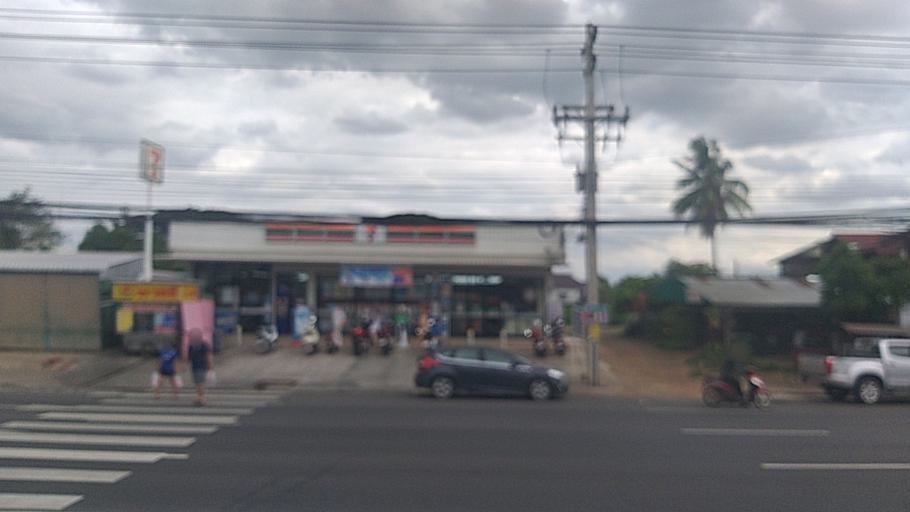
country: TH
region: Buriram
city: Nang Rong
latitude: 14.6340
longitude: 102.7876
